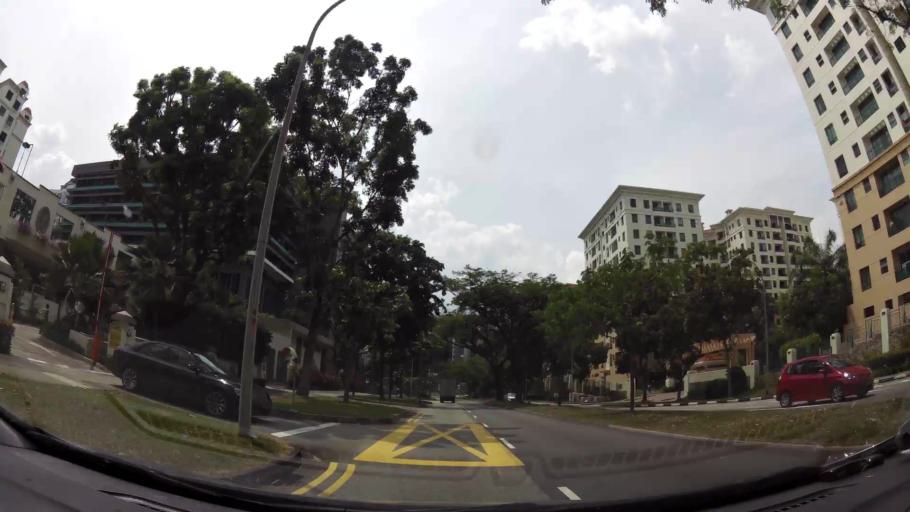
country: MY
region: Johor
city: Johor Bahru
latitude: 1.3583
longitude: 103.7632
